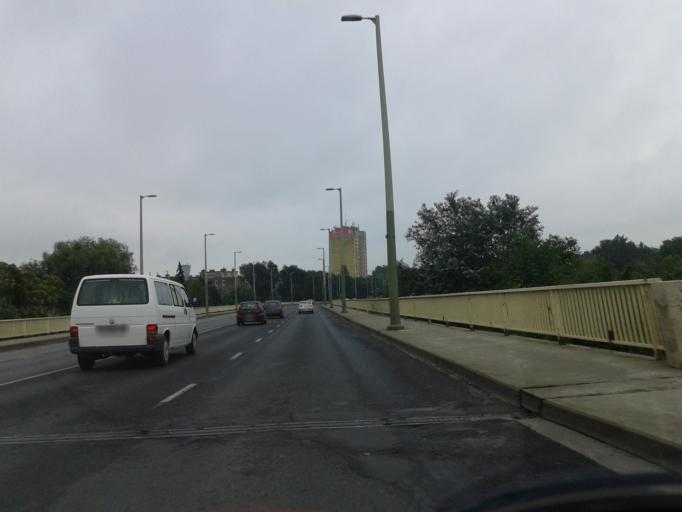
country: HU
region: Csongrad
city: Szeged
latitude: 46.2545
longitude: 20.1658
